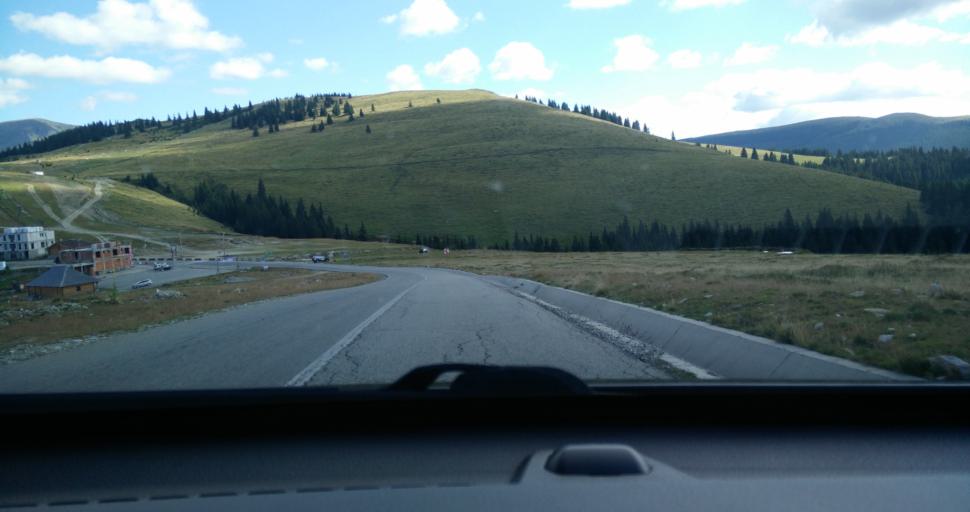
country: RO
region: Gorj
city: Novaci-Straini
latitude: 45.2735
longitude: 23.6889
